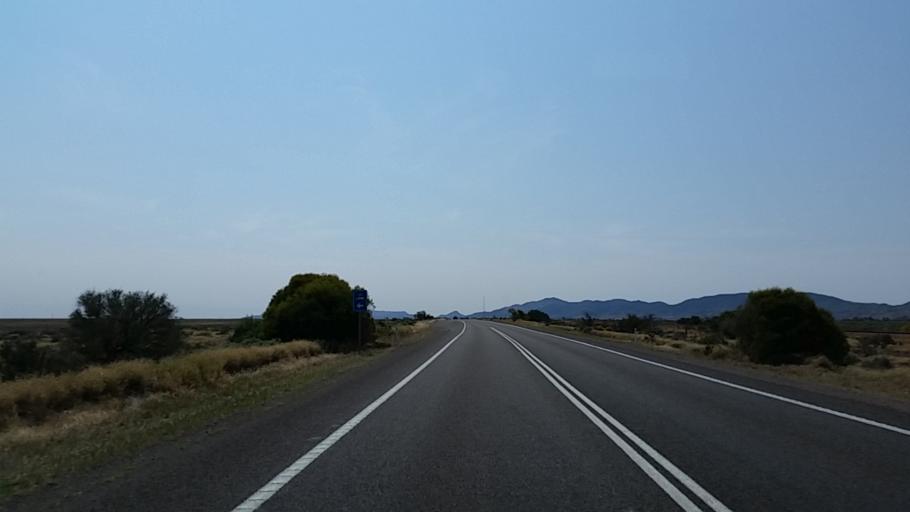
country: AU
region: South Australia
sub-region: Port Augusta
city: Port Augusta
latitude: -32.7086
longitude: 137.9415
